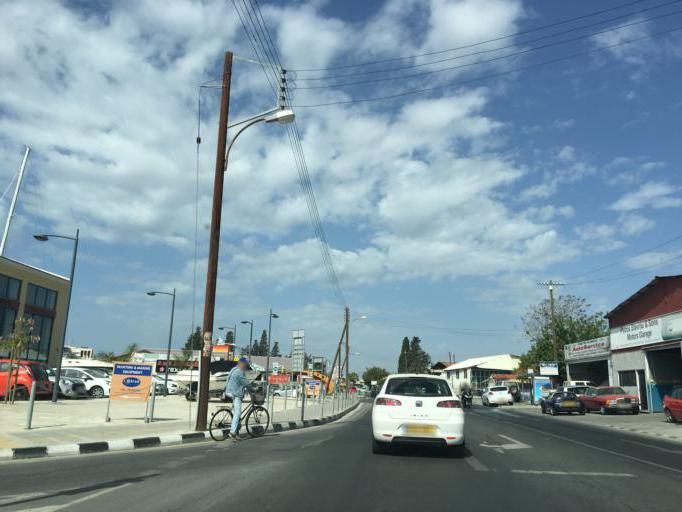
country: CY
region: Limassol
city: Limassol
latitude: 34.6718
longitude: 33.0371
